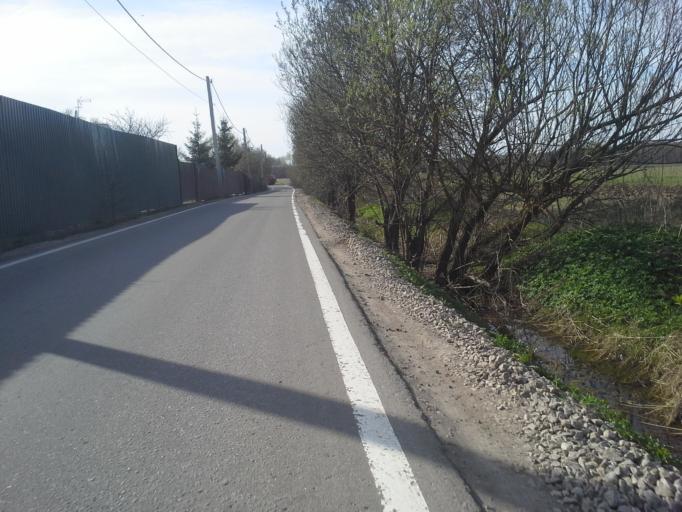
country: RU
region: Moskovskaya
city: Vatutinki
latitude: 55.4616
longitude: 37.3791
